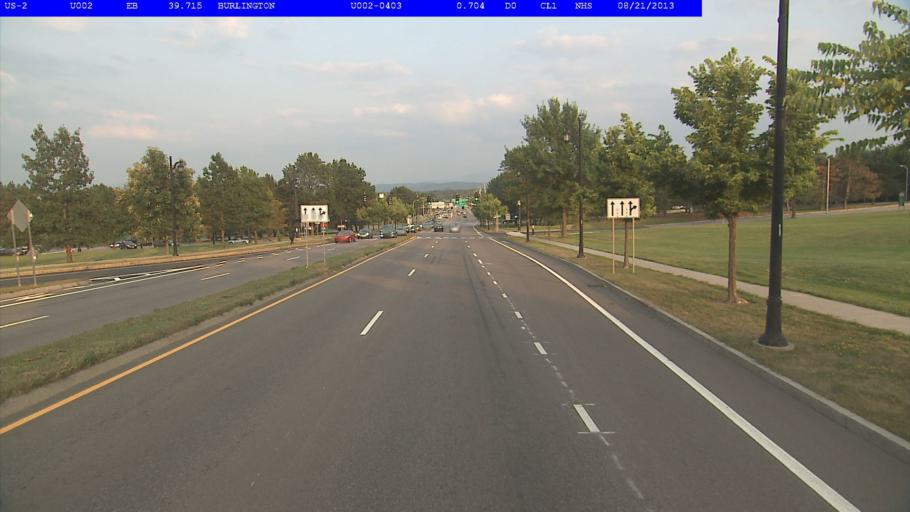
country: US
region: Vermont
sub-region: Chittenden County
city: Winooski
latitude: 44.4734
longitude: -73.1924
